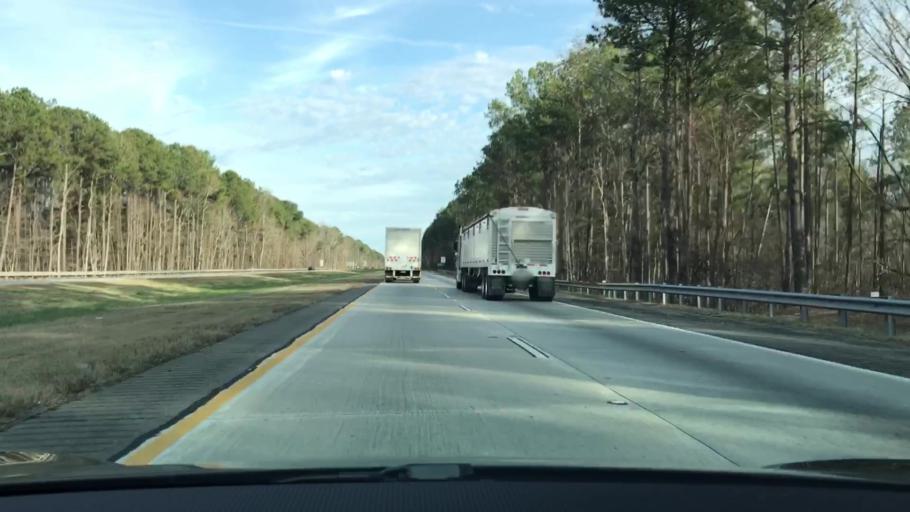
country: US
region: Georgia
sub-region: Greene County
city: Greensboro
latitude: 33.5465
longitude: -83.1916
